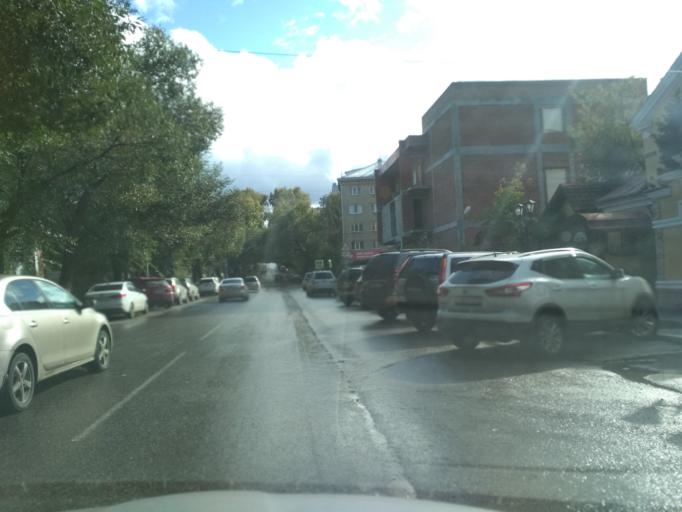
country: RU
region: Tomsk
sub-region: Tomskiy Rayon
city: Tomsk
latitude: 56.4823
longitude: 84.9515
